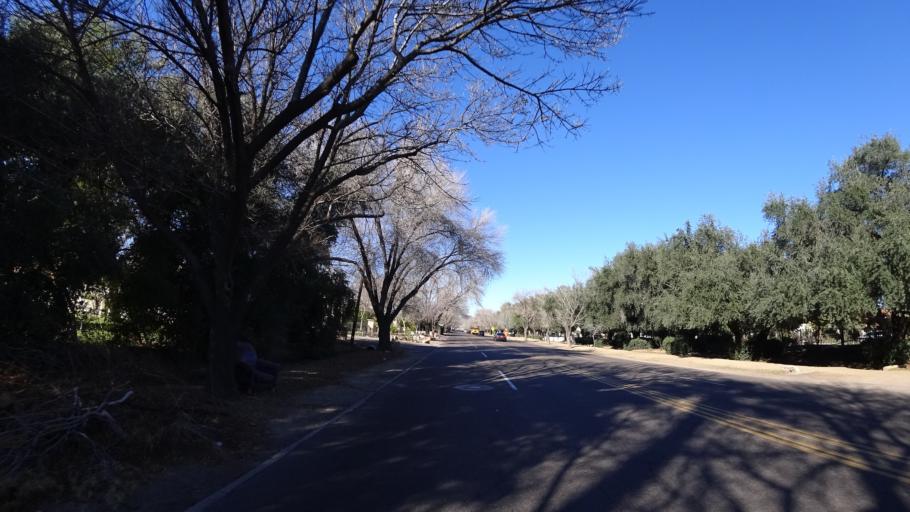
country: US
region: Arizona
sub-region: Maricopa County
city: Phoenix
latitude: 33.5321
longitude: -112.0738
